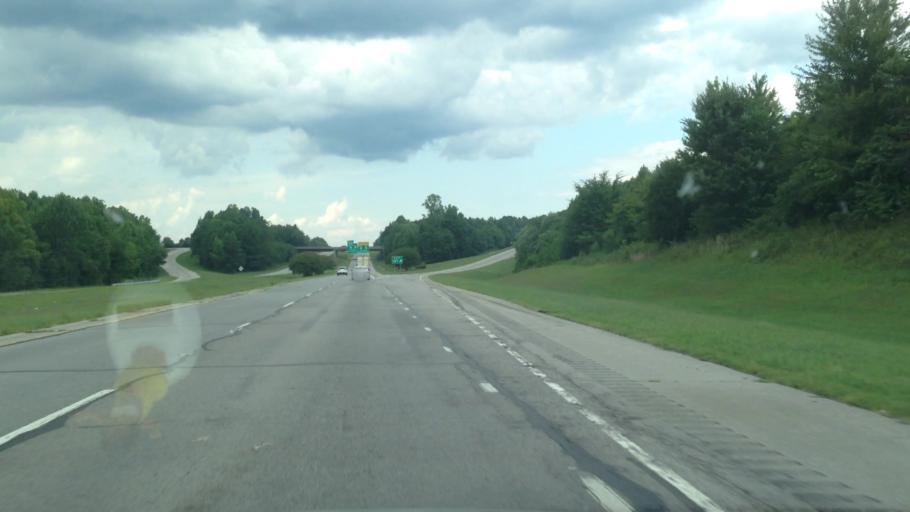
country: US
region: Virginia
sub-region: City of Danville
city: Danville
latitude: 36.5140
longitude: -79.4760
